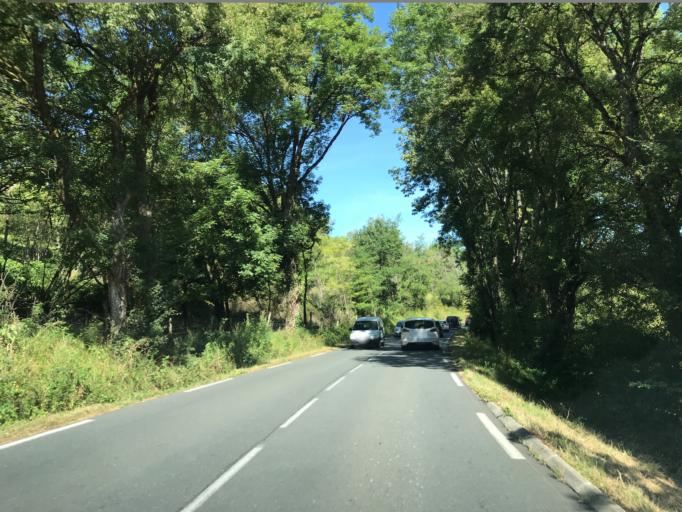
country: FR
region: Limousin
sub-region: Departement de la Correze
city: Larche
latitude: 45.1014
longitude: 1.3878
